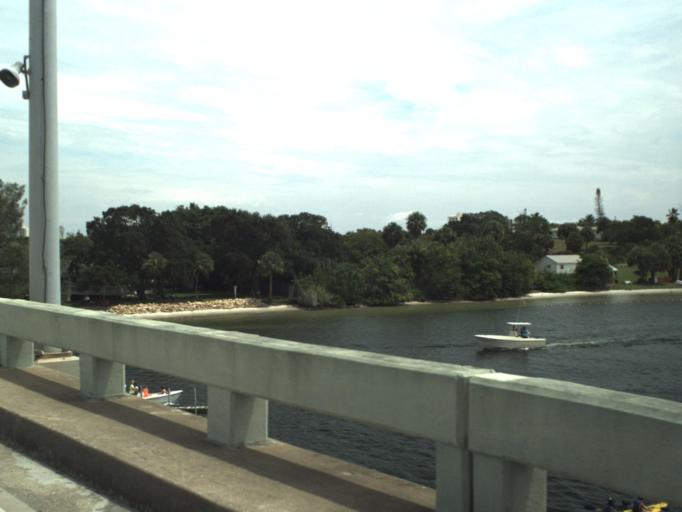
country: US
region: Florida
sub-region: Palm Beach County
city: Jupiter
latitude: 26.9470
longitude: -80.0848
